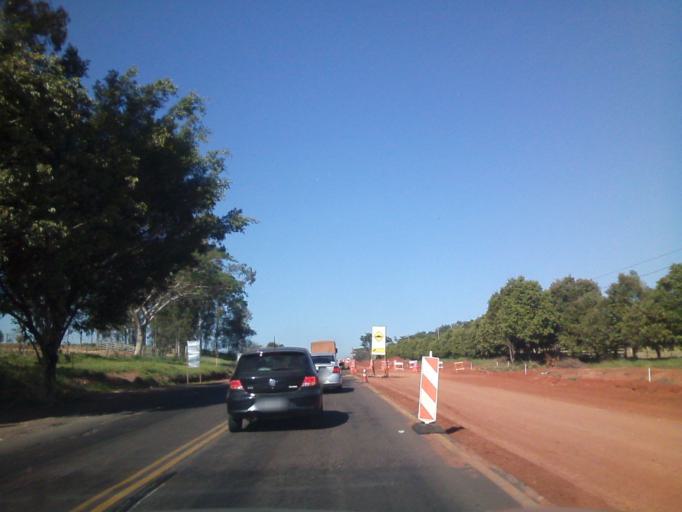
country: BR
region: Sao Paulo
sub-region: Pirapozinho
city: Pirapozinho
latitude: -22.2237
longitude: -51.4406
